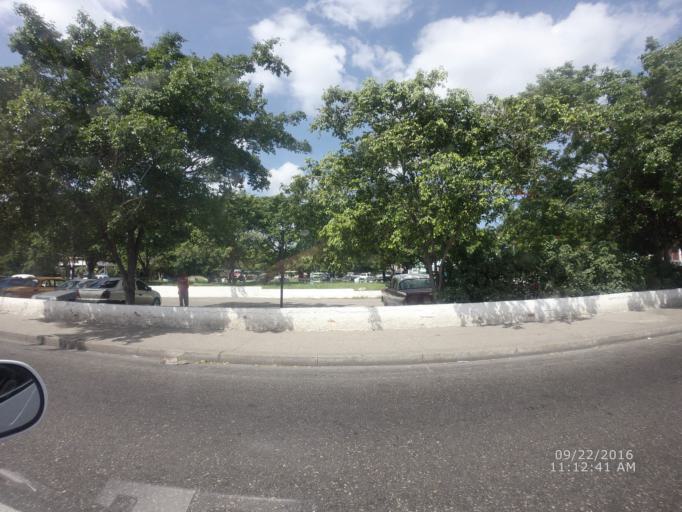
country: CU
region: La Habana
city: Cerro
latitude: 23.0932
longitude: -82.4217
